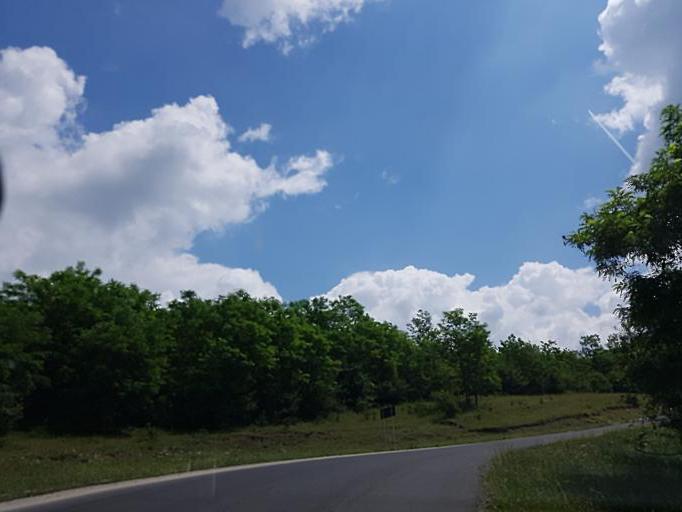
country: RO
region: Sibiu
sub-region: Comuna Seica Mica
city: Seica Mica
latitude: 46.0480
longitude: 24.1553
